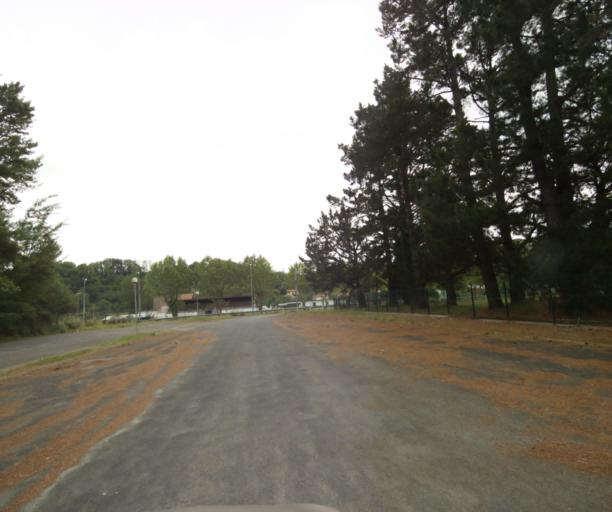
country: FR
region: Aquitaine
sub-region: Departement des Pyrenees-Atlantiques
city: Mouguerre
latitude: 43.4861
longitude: -1.4300
